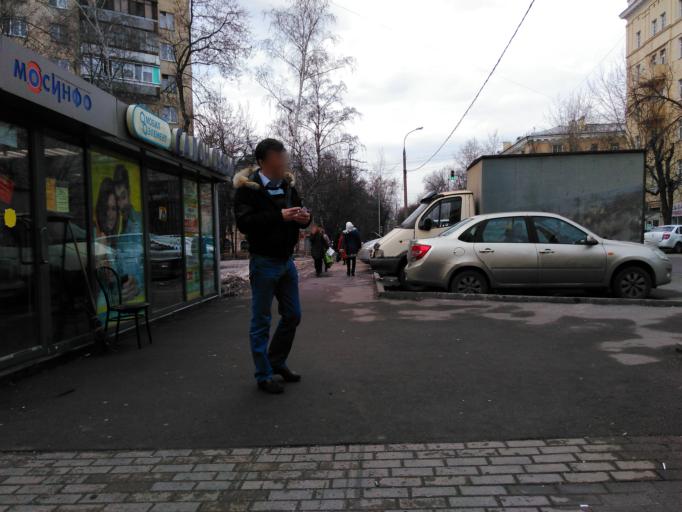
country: RU
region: Moscow
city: Vatutino
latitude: 55.8641
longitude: 37.6810
